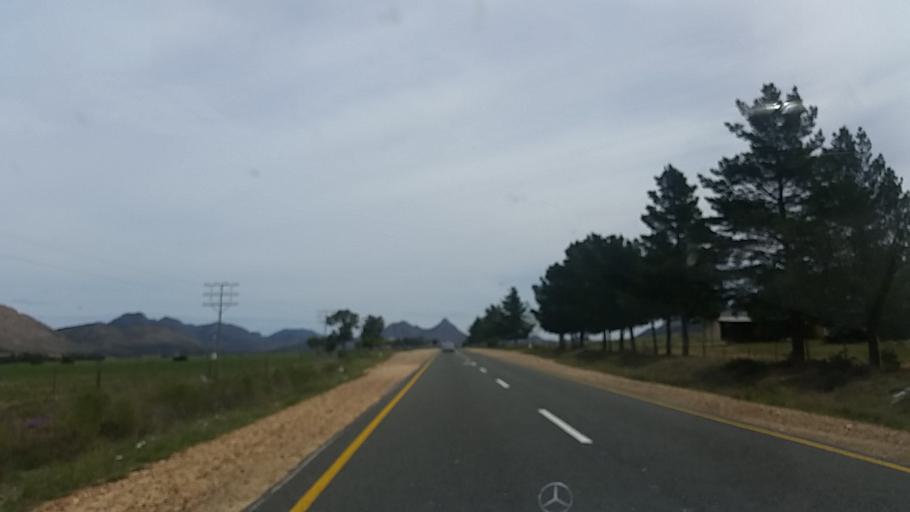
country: ZA
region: Western Cape
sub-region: Eden District Municipality
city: George
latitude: -33.8169
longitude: 22.5109
